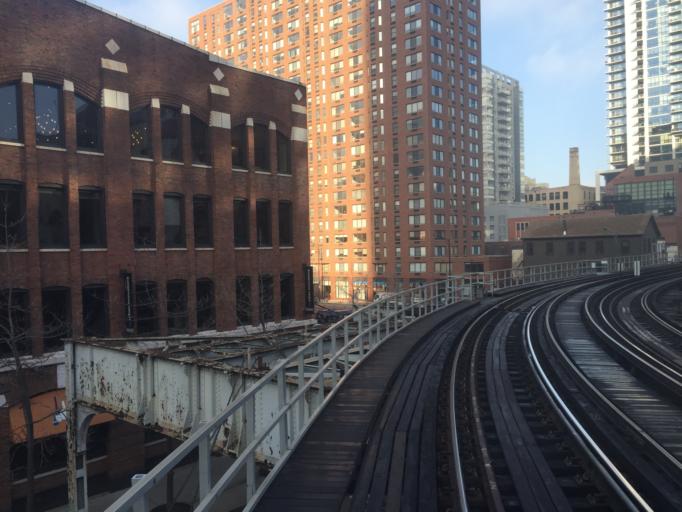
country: US
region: Illinois
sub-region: Cook County
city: Chicago
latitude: 41.8903
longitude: -87.6355
